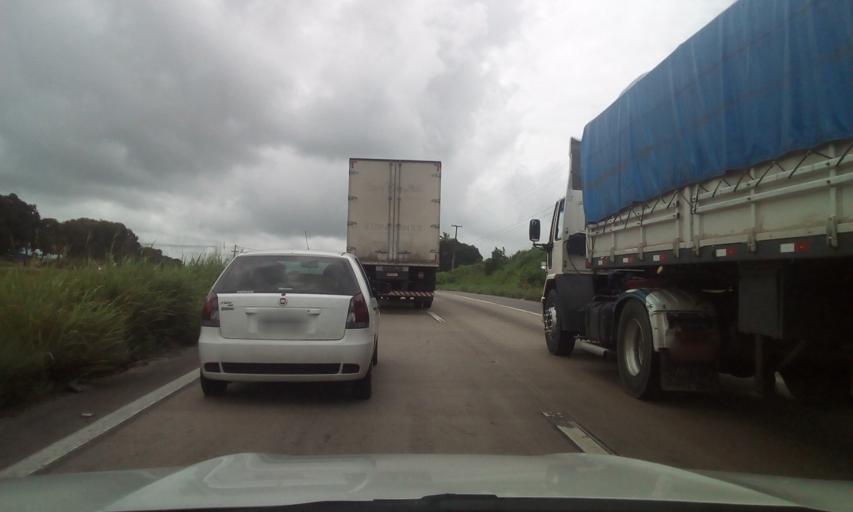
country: BR
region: Pernambuco
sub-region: Igarassu
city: Igarassu
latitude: -7.8012
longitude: -34.9262
